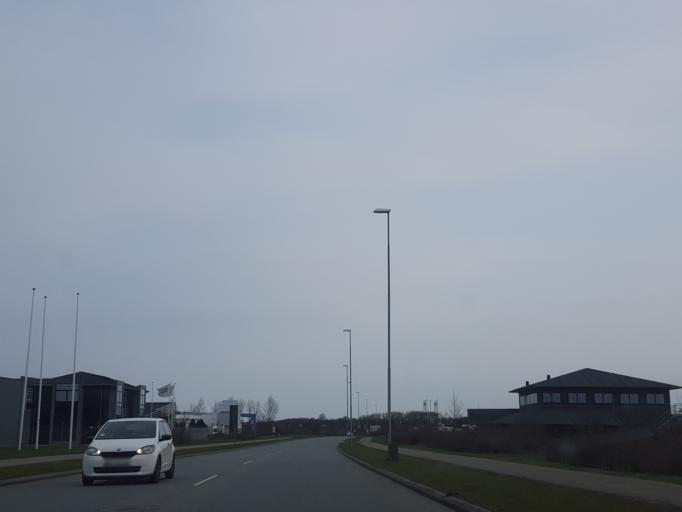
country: DK
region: South Denmark
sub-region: Esbjerg Kommune
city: Esbjerg
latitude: 55.5139
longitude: 8.4670
